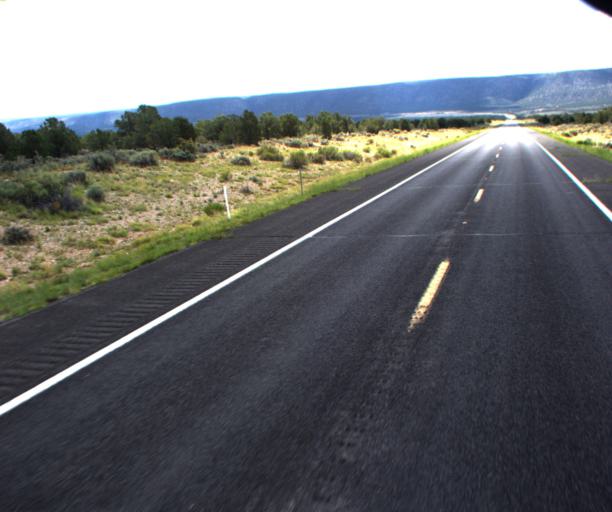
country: US
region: Arizona
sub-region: Coconino County
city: Grand Canyon
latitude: 35.9467
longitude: -111.7789
